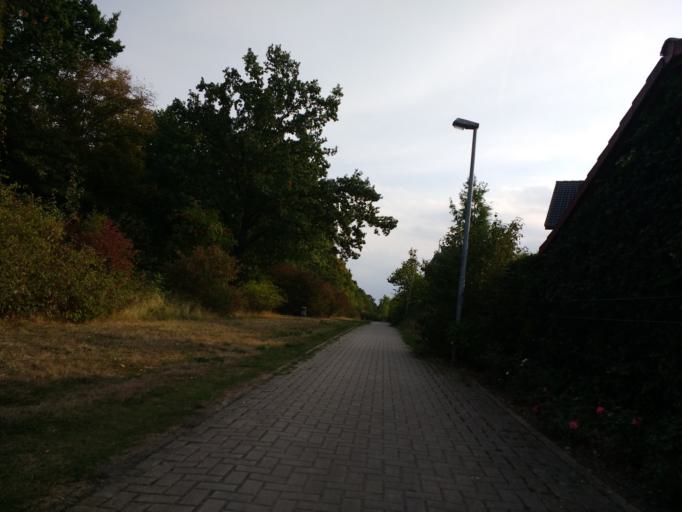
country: DE
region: Lower Saxony
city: Wolfsburg
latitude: 52.4161
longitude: 10.7455
